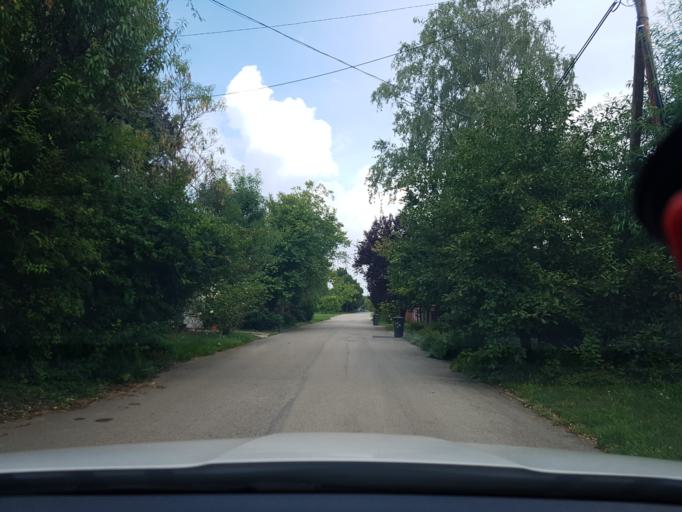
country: HU
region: Veszprem
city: Balatonalmadi
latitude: 46.9897
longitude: 17.9831
